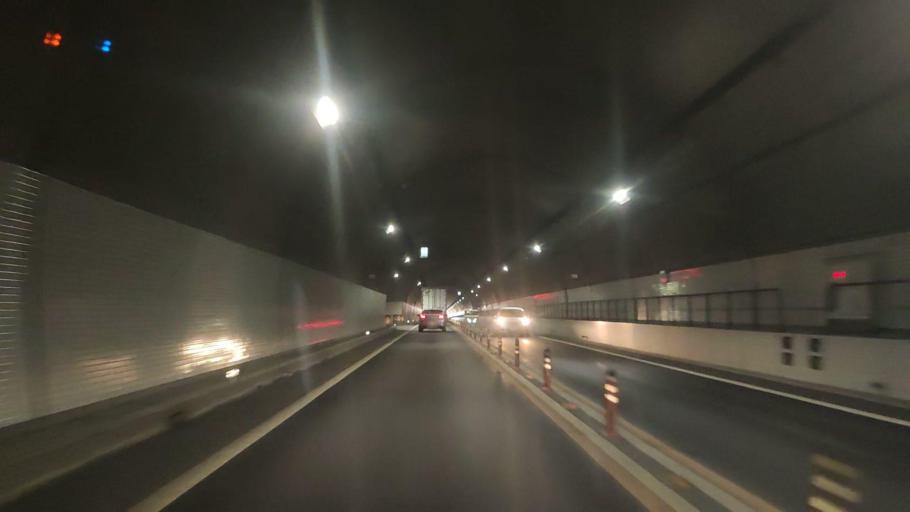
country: JP
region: Fukuoka
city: Kanda
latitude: 33.7646
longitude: 130.9632
